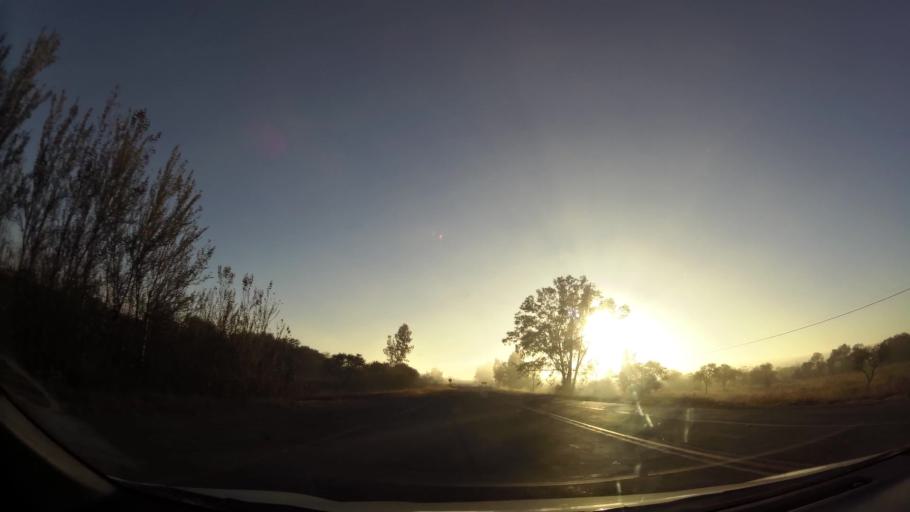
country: ZA
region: Limpopo
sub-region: Capricorn District Municipality
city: Polokwane
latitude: -23.9851
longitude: 29.3586
